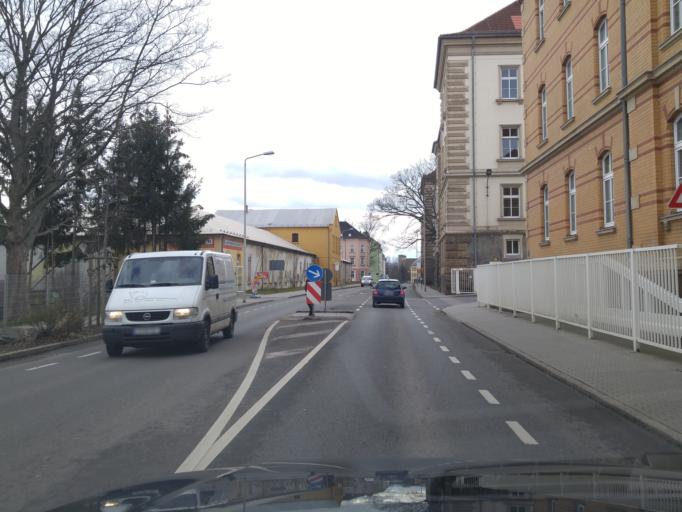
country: DE
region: Saxony
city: Weissenborn
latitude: 50.7232
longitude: 12.4759
